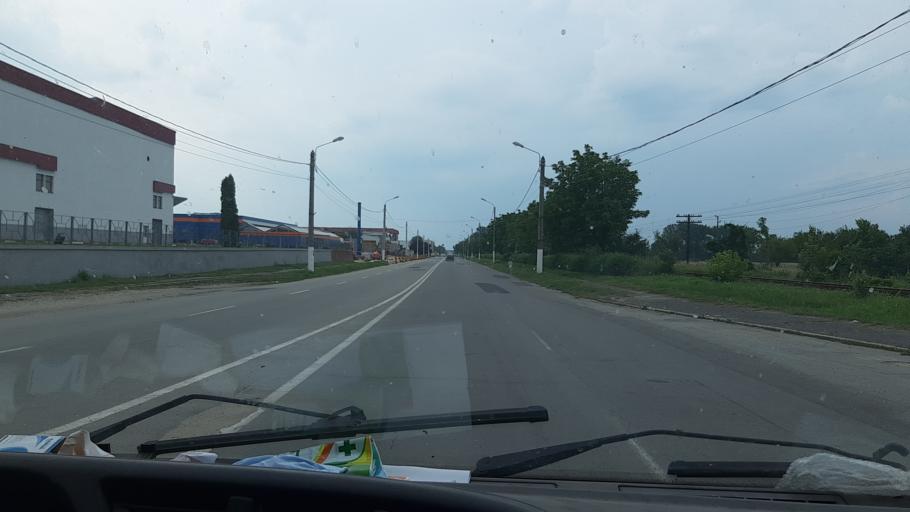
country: RO
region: Timis
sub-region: Municipiul Lugoj
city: Lugoj
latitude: 45.7023
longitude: 21.8926
